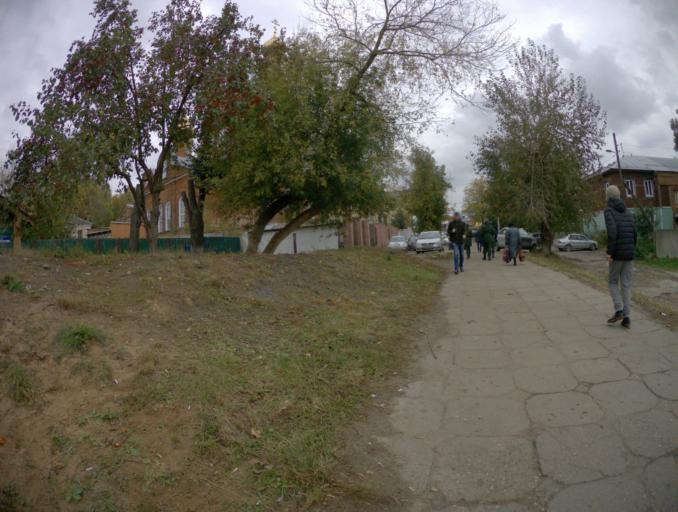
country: RU
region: Vladimir
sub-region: Kovrovskiy Rayon
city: Kovrov
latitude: 56.3677
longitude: 41.3036
